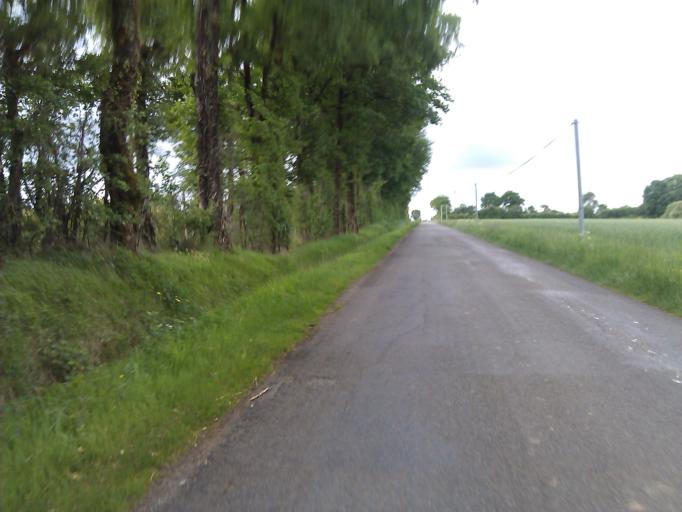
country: FR
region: Poitou-Charentes
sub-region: Departement de la Vienne
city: Charroux
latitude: 46.0967
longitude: 0.5127
